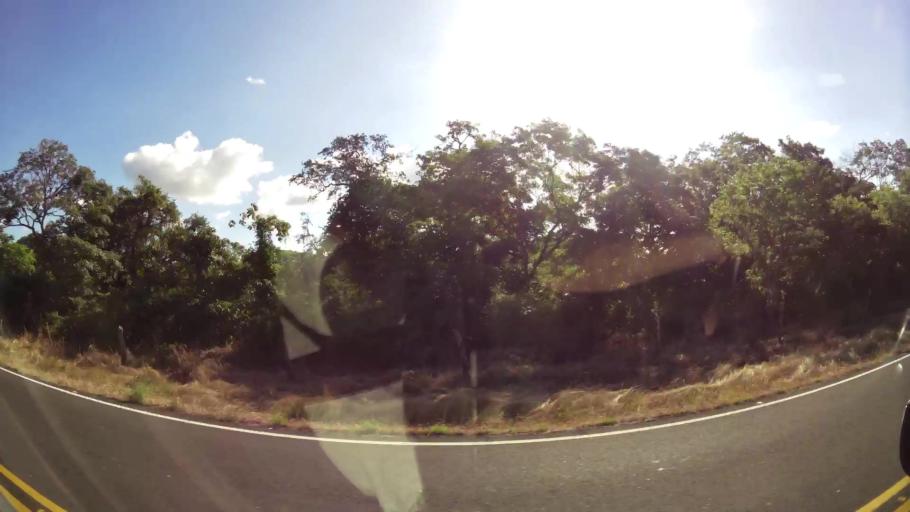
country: CR
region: Guanacaste
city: Sardinal
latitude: 10.5882
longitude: -85.6391
